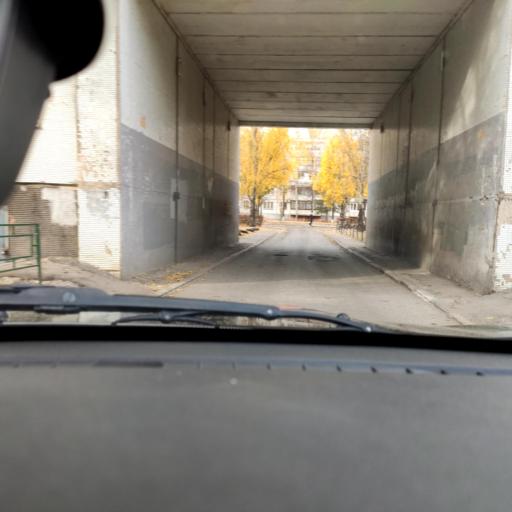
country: RU
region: Samara
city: Tol'yatti
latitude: 53.5196
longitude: 49.3042
